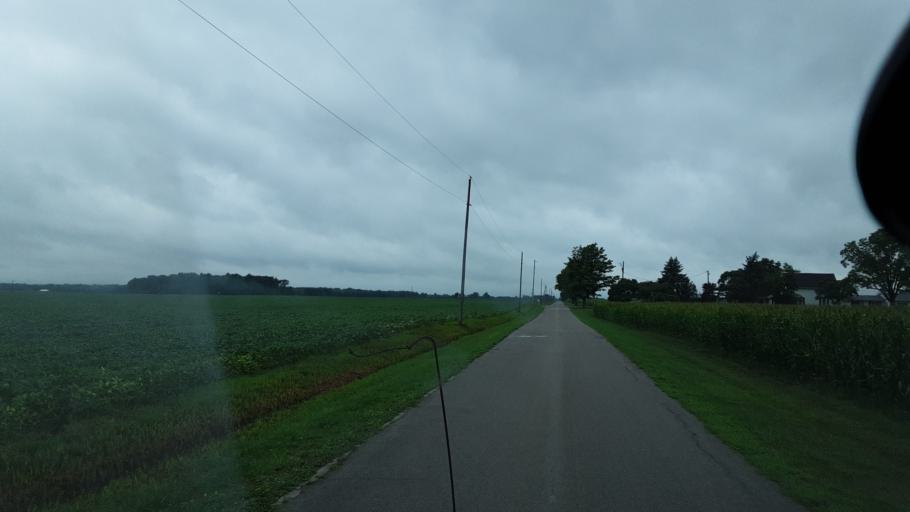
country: US
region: Ohio
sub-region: Van Wert County
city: Convoy
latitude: 40.8296
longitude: -84.7555
